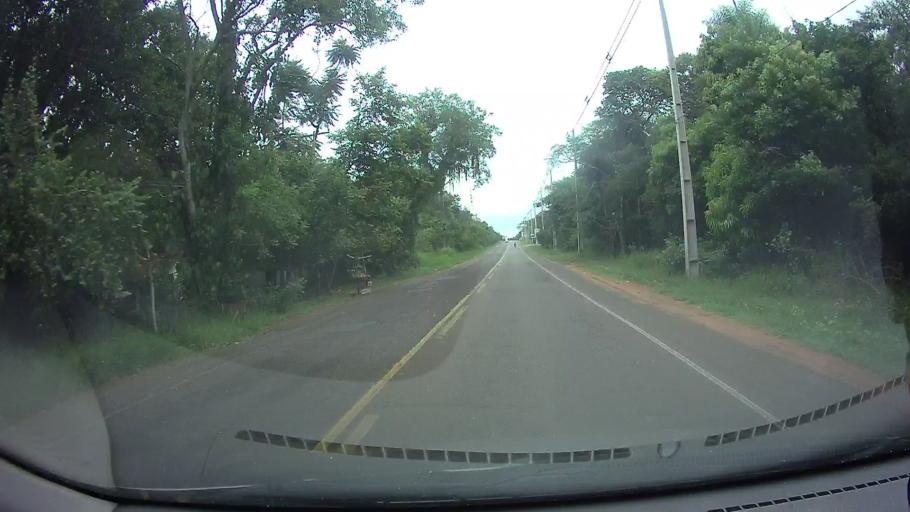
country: PY
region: Cordillera
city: Altos
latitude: -25.2767
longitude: -57.2609
